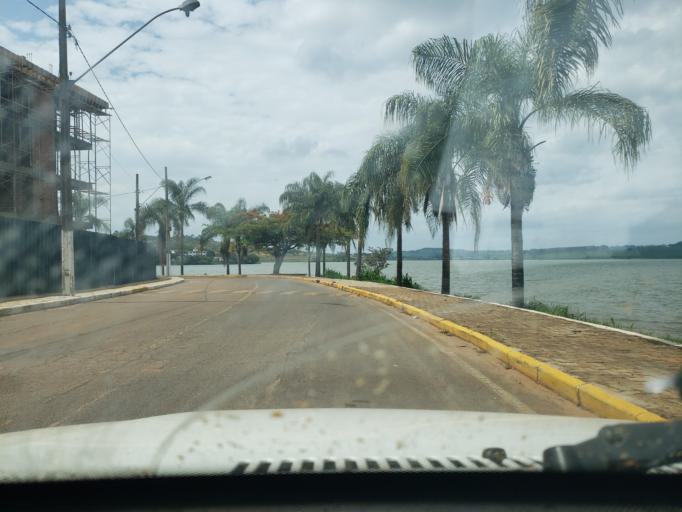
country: BR
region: Minas Gerais
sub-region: Boa Esperanca
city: Boa Esperanca
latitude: -21.0840
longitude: -45.5700
